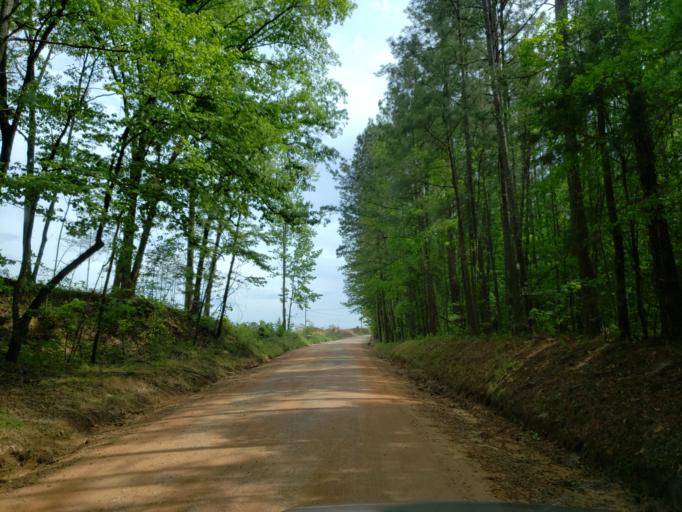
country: US
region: Georgia
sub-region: Monroe County
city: Forsyth
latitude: 32.9835
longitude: -83.9139
